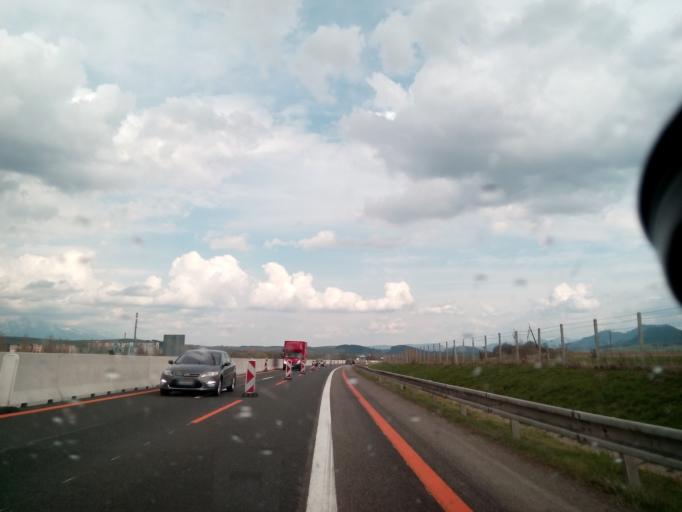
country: SK
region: Zilinsky
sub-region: Okres Liptovsky Mikulas
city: Liptovsky Mikulas
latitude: 49.0729
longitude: 19.6124
